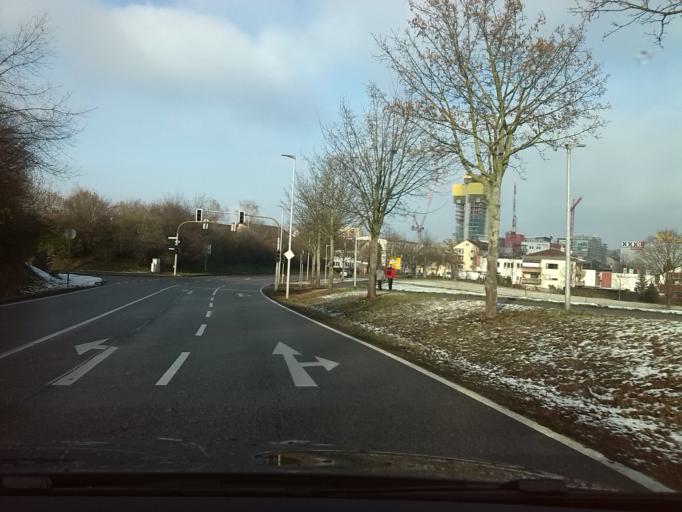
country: DE
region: Baden-Wuerttemberg
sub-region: Regierungsbezirk Stuttgart
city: Fellbach
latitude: 48.8124
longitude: 9.2858
